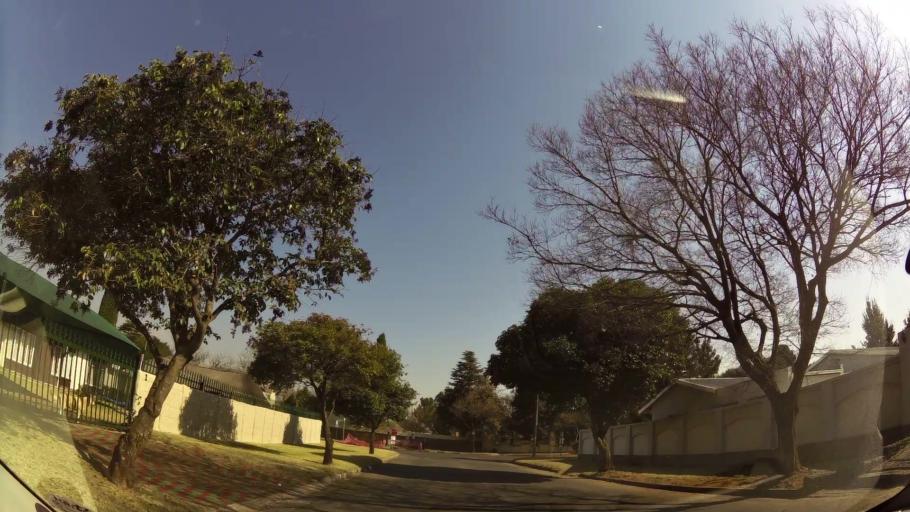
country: ZA
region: Gauteng
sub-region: Ekurhuleni Metropolitan Municipality
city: Boksburg
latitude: -26.1635
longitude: 28.2652
